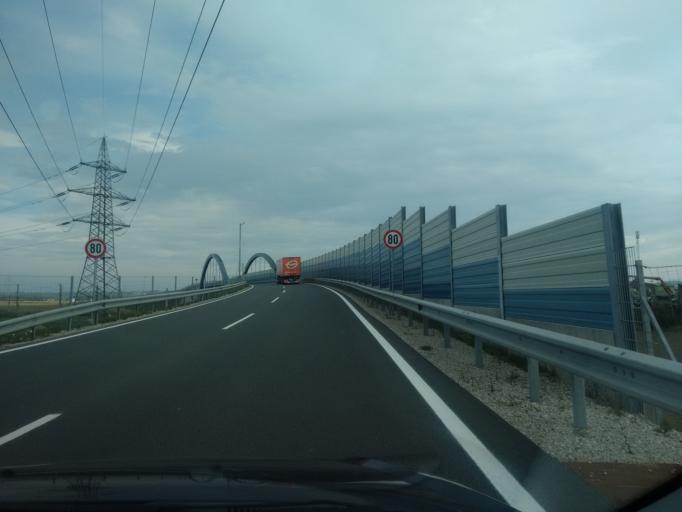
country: AT
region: Upper Austria
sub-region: Wels-Land
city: Edt bei Lambach
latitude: 48.1027
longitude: 13.8984
